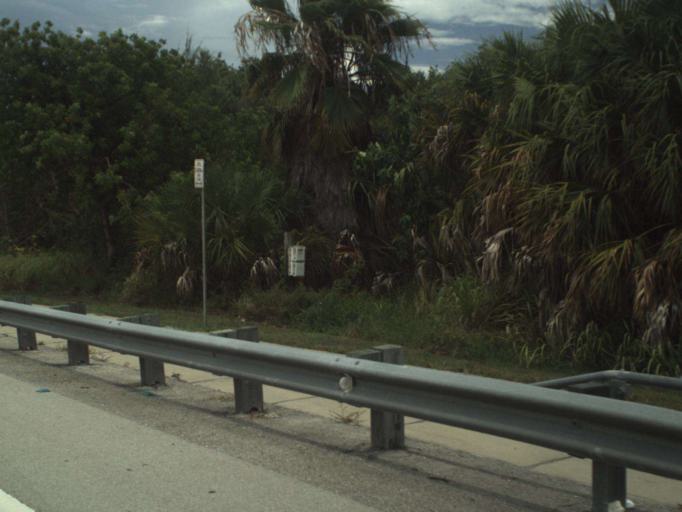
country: US
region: Florida
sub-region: Saint Lucie County
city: Hutchinson Island South
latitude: 27.3517
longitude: -80.2444
